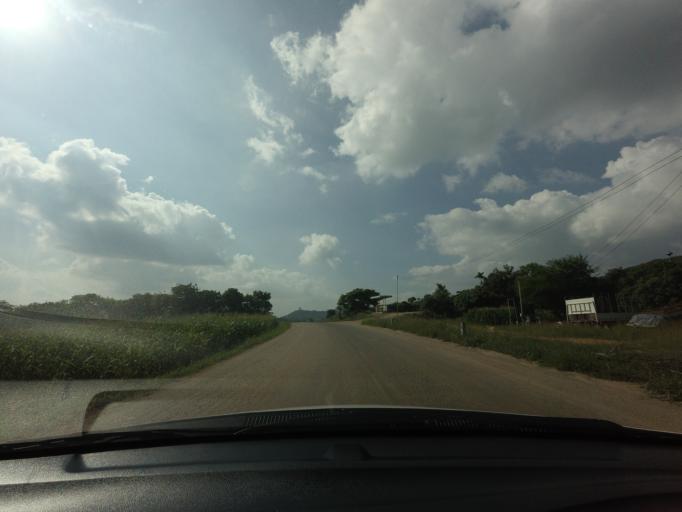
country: TH
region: Nakhon Ratchasima
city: Pak Chong
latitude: 14.5483
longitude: 101.6220
